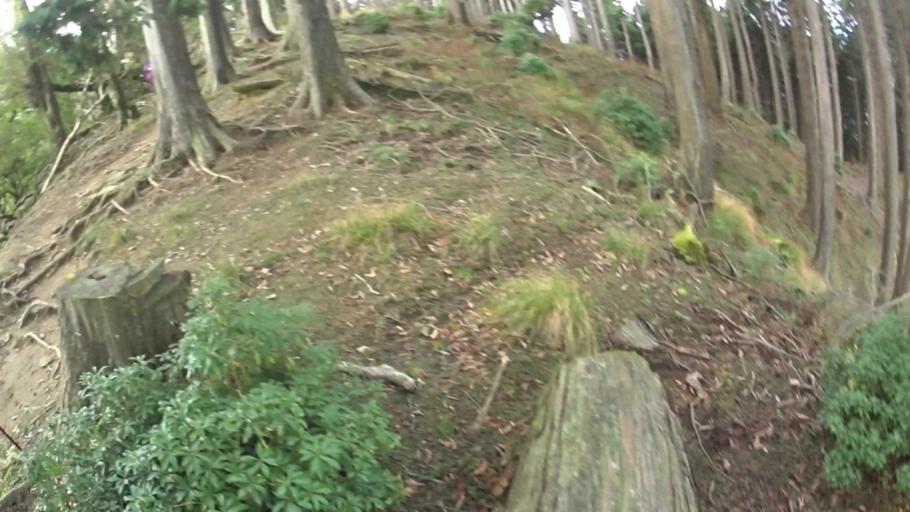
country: JP
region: Shiga Prefecture
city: Otsu-shi
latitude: 35.0954
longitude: 135.8378
